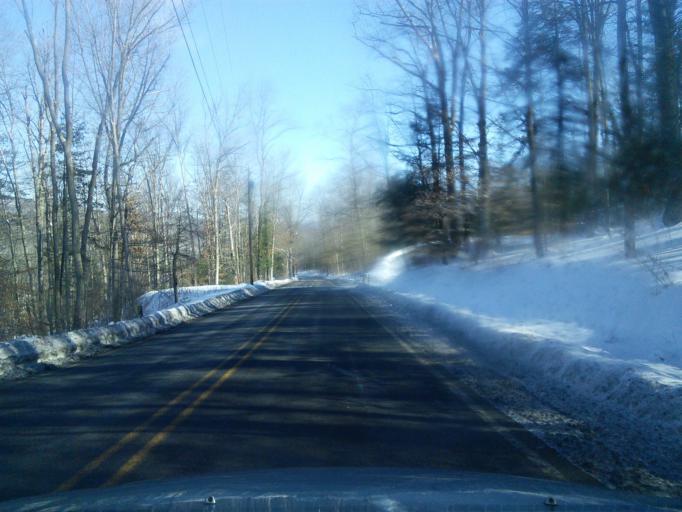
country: US
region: Pennsylvania
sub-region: Centre County
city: Park Forest Village
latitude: 40.8585
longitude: -77.9347
